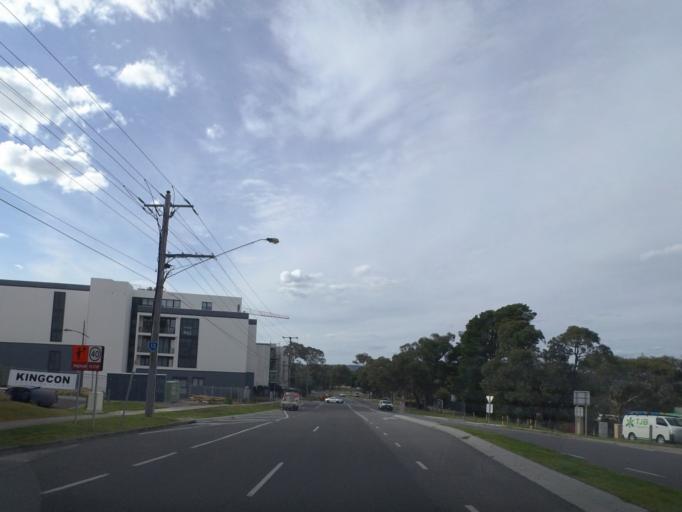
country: AU
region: Victoria
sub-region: Manningham
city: Donvale
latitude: -37.7637
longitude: 145.1728
